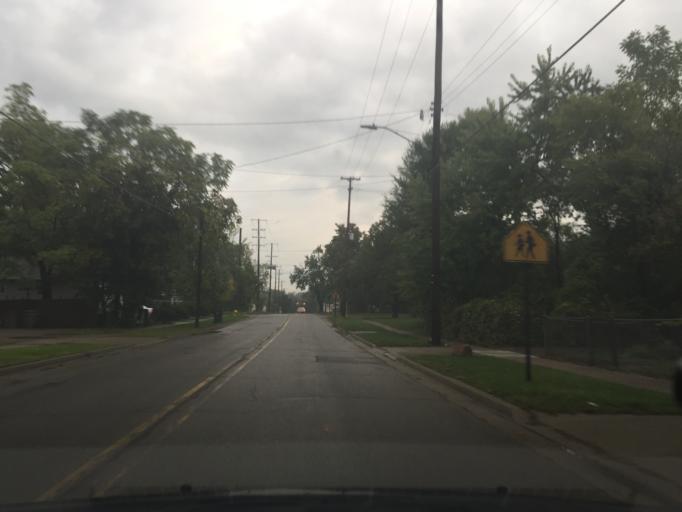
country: US
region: Michigan
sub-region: Oakland County
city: Pontiac
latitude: 42.6358
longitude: -83.2823
